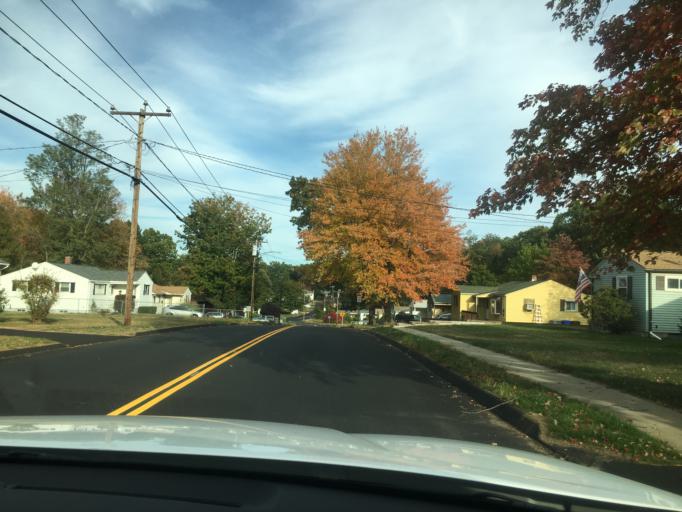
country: US
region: Connecticut
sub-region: Hartford County
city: Sherwood Manor
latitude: 42.0251
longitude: -72.5641
